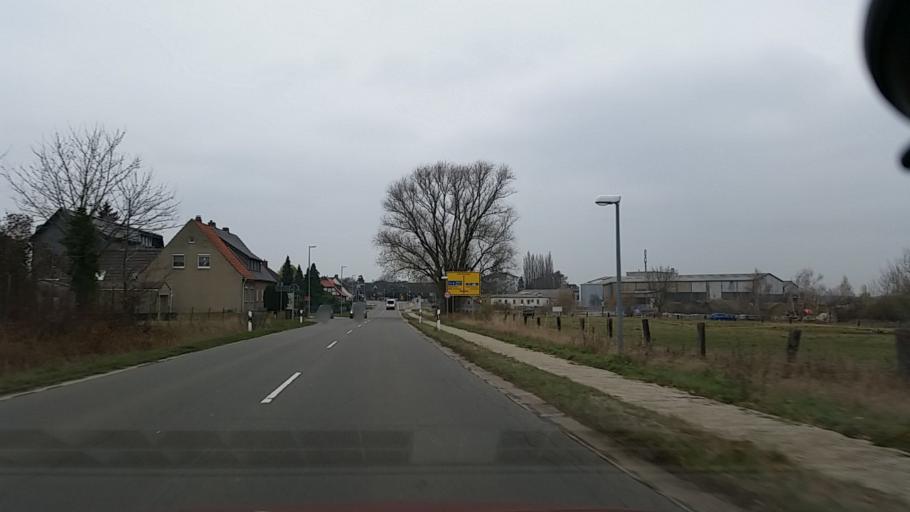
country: DE
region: Lower Saxony
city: Danndorf
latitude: 52.4174
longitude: 10.8516
